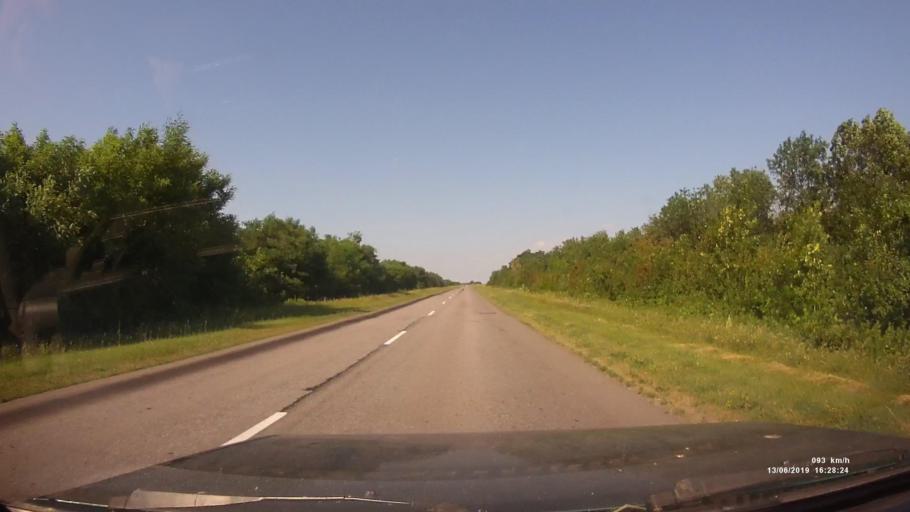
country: RU
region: Rostov
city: Kazanskaya
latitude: 49.8213
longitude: 41.1993
